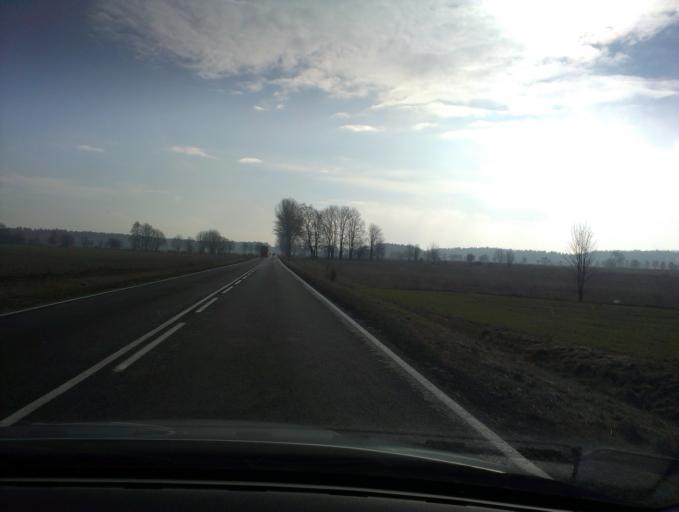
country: PL
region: West Pomeranian Voivodeship
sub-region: Powiat koszalinski
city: Bobolice
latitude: 54.0216
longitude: 16.4774
